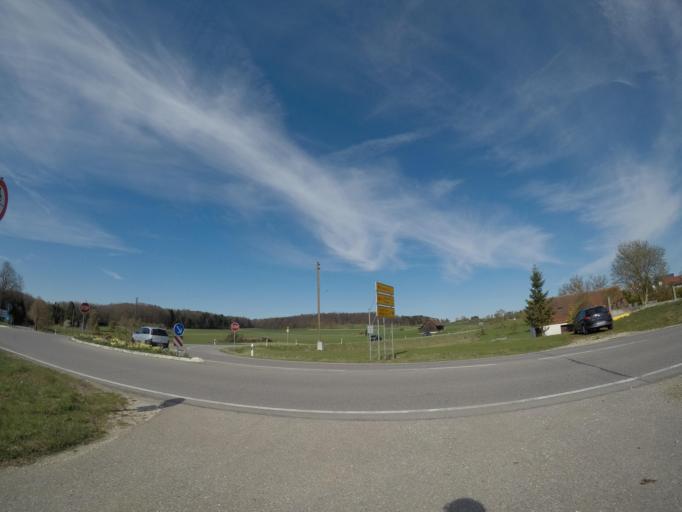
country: DE
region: Baden-Wuerttemberg
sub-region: Tuebingen Region
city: Mehrstetten
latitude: 48.3289
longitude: 9.6003
